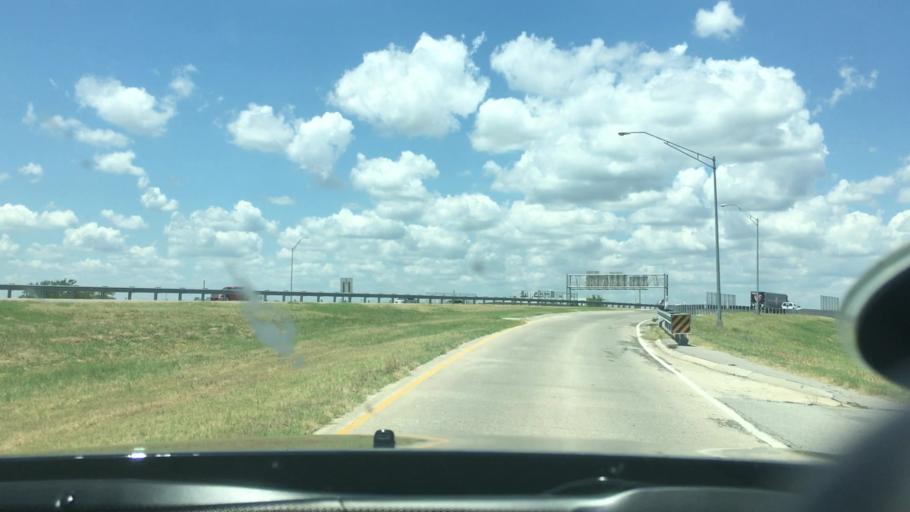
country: US
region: Oklahoma
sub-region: Carter County
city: Ardmore
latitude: 34.1757
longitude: -97.1674
